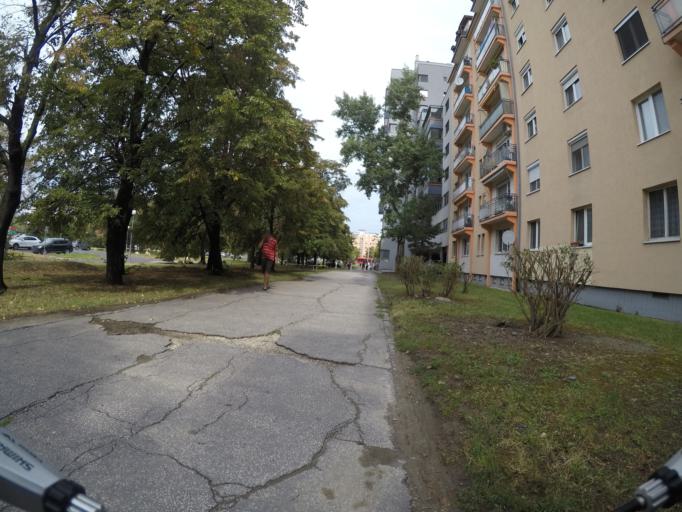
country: SK
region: Bratislavsky
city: Bratislava
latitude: 48.1554
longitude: 17.1564
